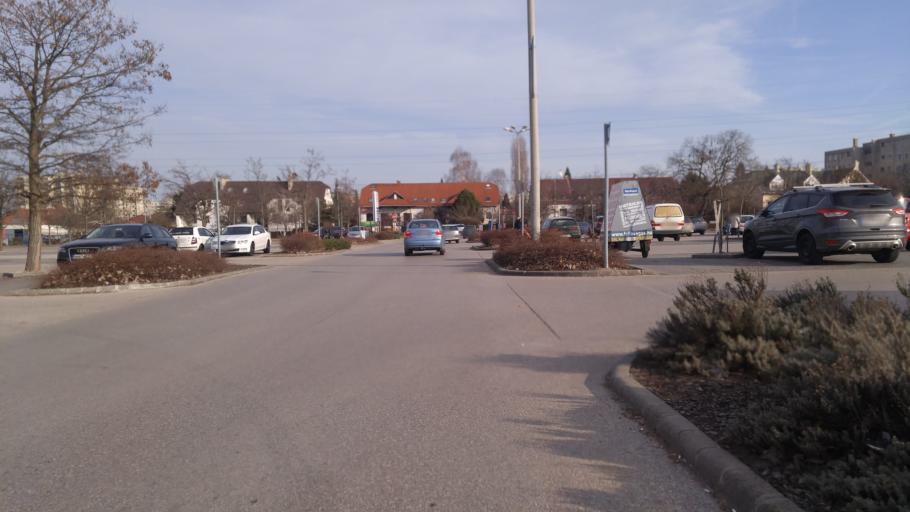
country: HU
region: Budapest
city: Budapest XVII. keruelet
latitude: 47.4837
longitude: 19.2290
